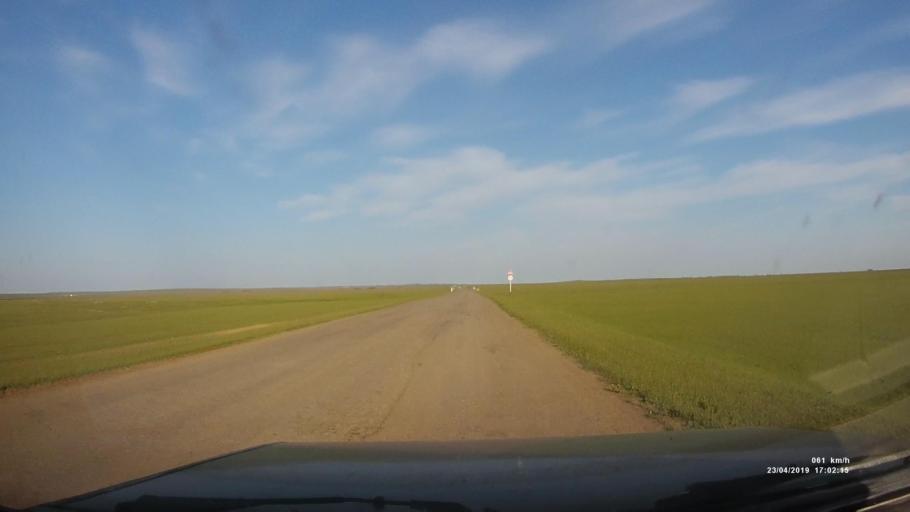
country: RU
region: Kalmykiya
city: Priyutnoye
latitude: 46.2932
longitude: 43.4154
